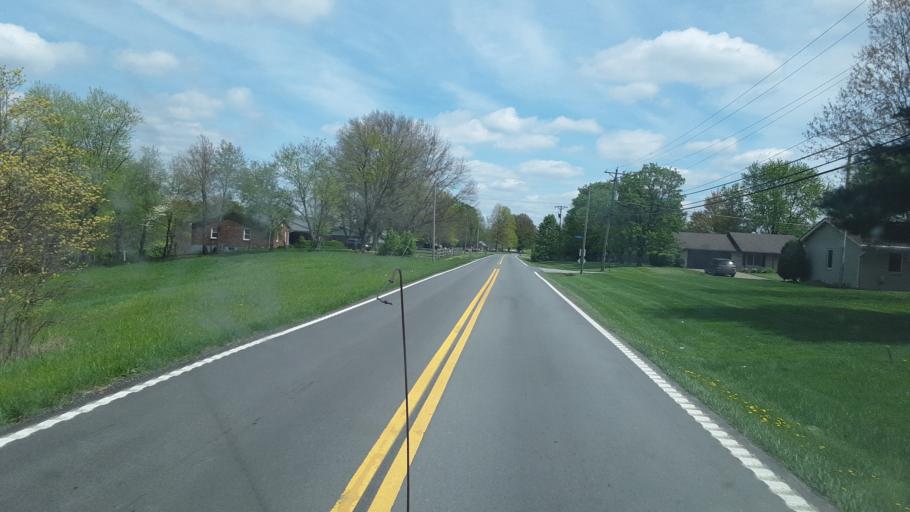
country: US
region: Kentucky
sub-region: Grant County
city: Dry Ridge
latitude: 38.6783
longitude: -84.6226
